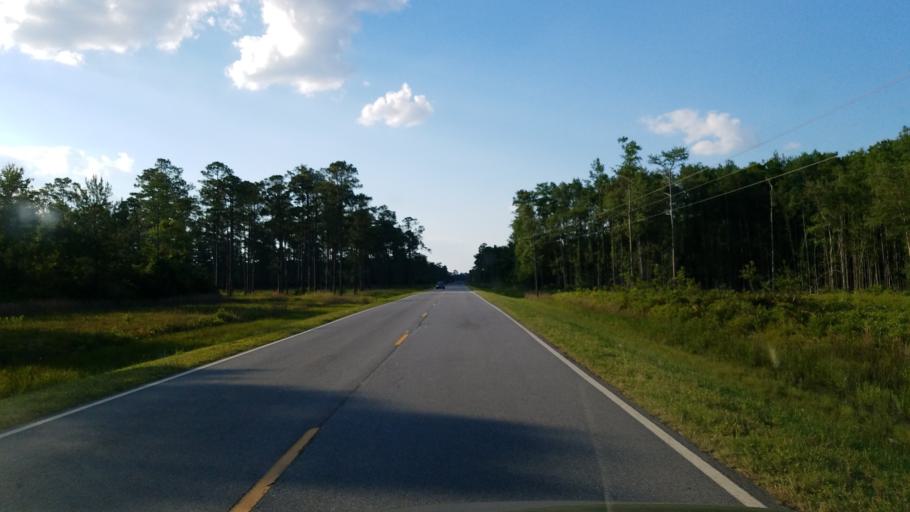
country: US
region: Georgia
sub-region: Lanier County
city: Lakeland
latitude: 31.1183
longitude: -83.0831
